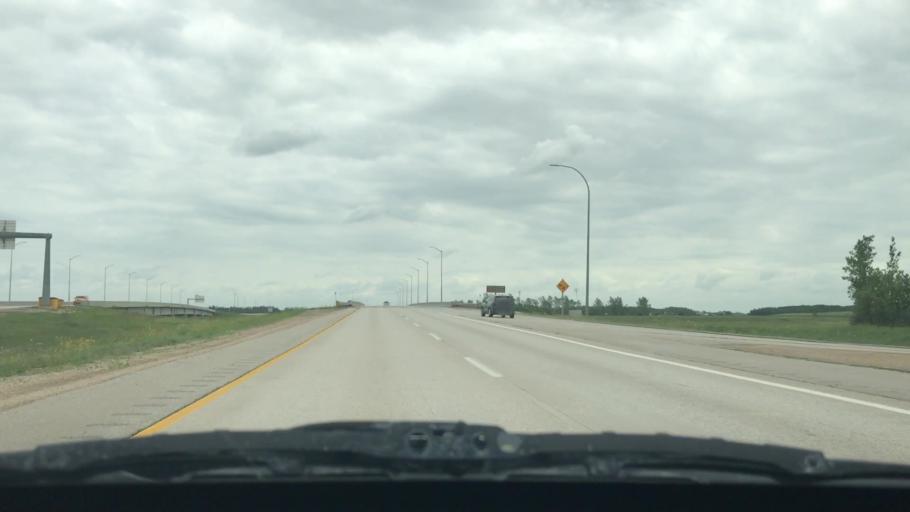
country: CA
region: Manitoba
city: Winnipeg
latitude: 49.8327
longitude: -96.9594
